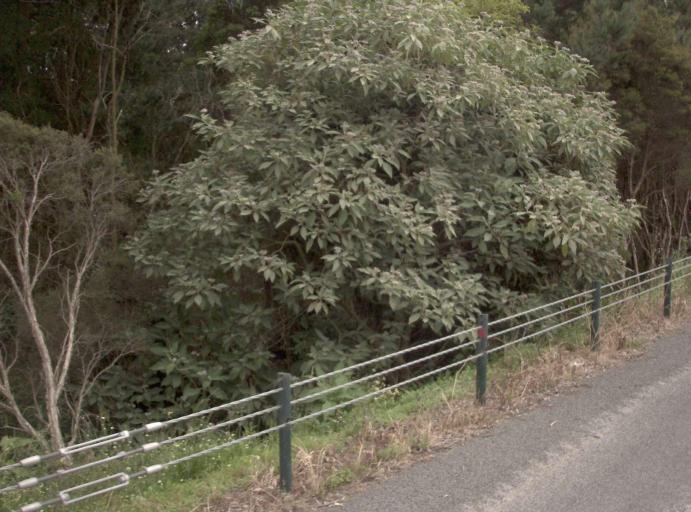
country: AU
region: Victoria
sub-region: Bass Coast
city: North Wonthaggi
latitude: -38.5648
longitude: 145.9645
